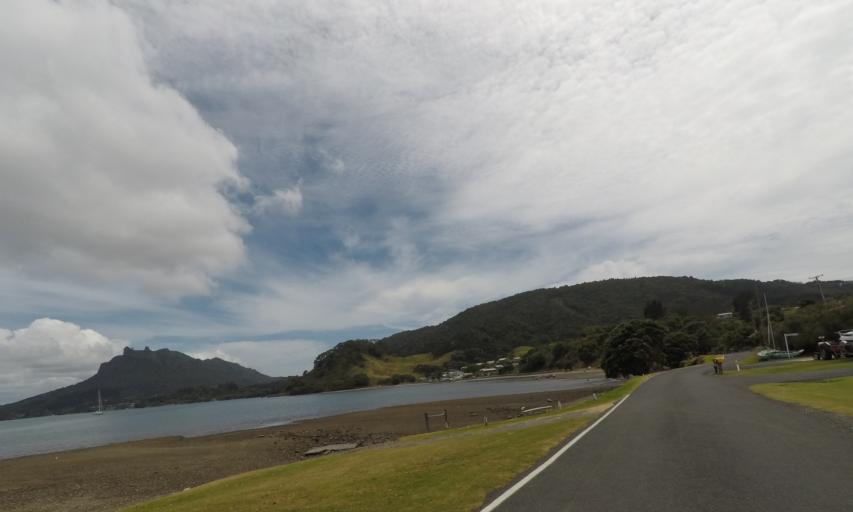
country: NZ
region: Northland
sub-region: Whangarei
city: Ruakaka
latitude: -35.8461
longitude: 174.5354
